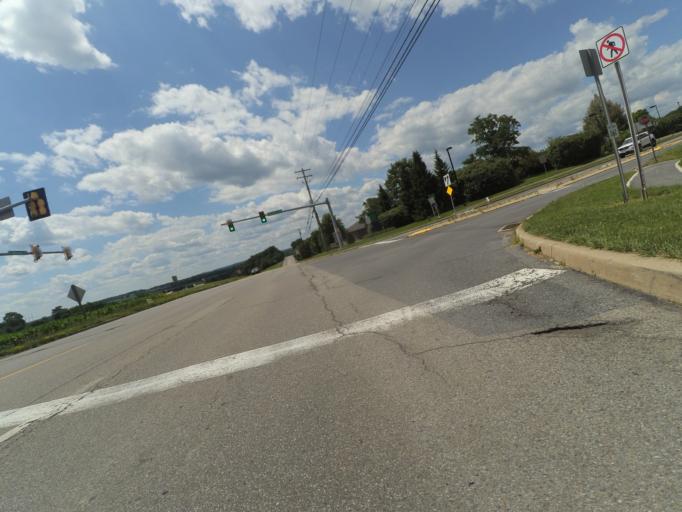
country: US
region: Pennsylvania
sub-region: Centre County
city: Lemont
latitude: 40.7834
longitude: -77.8186
